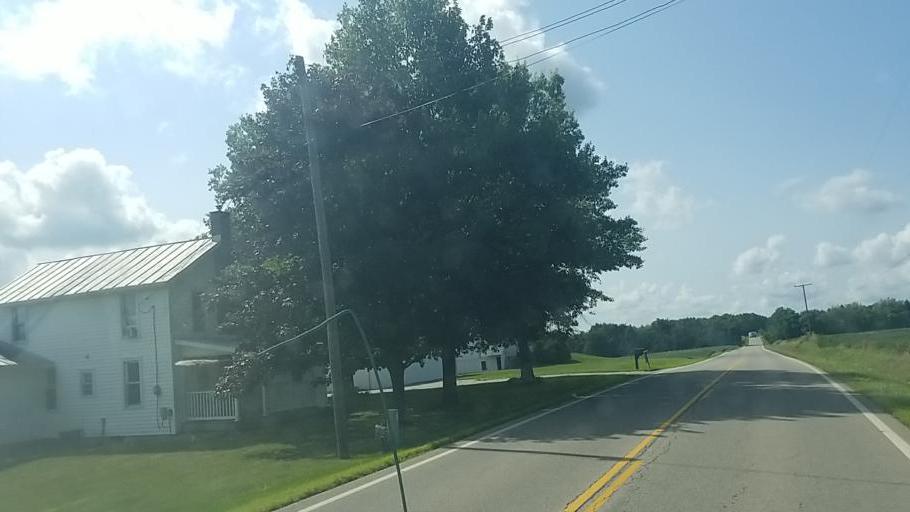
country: US
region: Ohio
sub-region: Ashland County
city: Ashland
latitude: 40.7613
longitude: -82.3070
